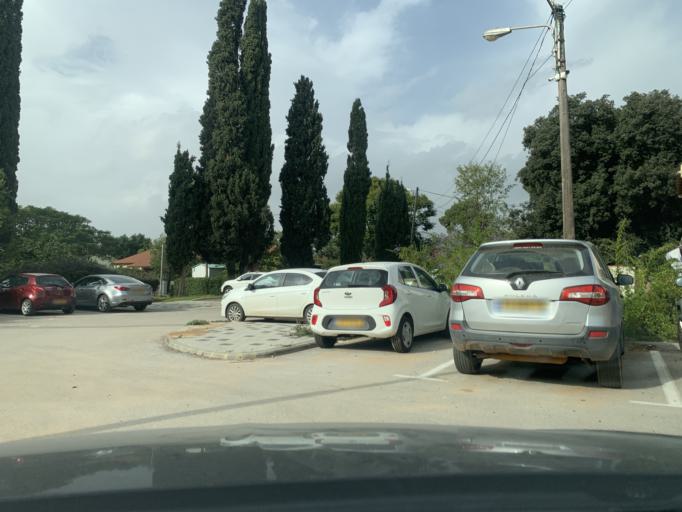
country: IL
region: Central District
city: Tirah
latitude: 32.2161
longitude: 34.9370
